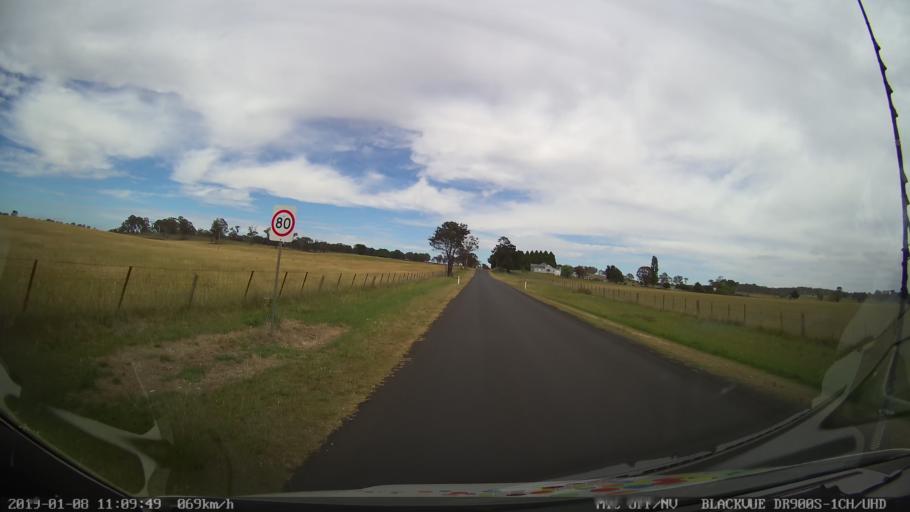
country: AU
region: New South Wales
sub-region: Guyra
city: Guyra
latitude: -30.2265
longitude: 151.6428
